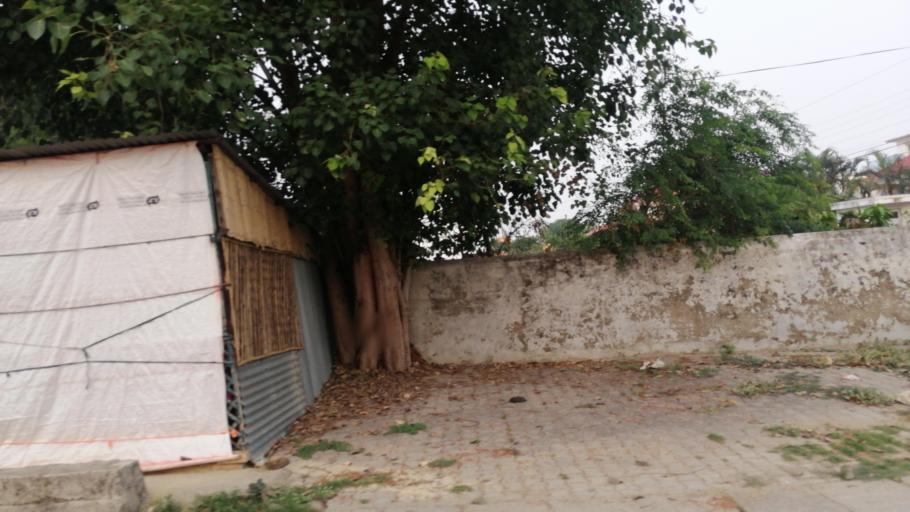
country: NP
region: Western Region
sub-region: Lumbini Zone
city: Bhairahawa
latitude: 27.4998
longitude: 83.4485
